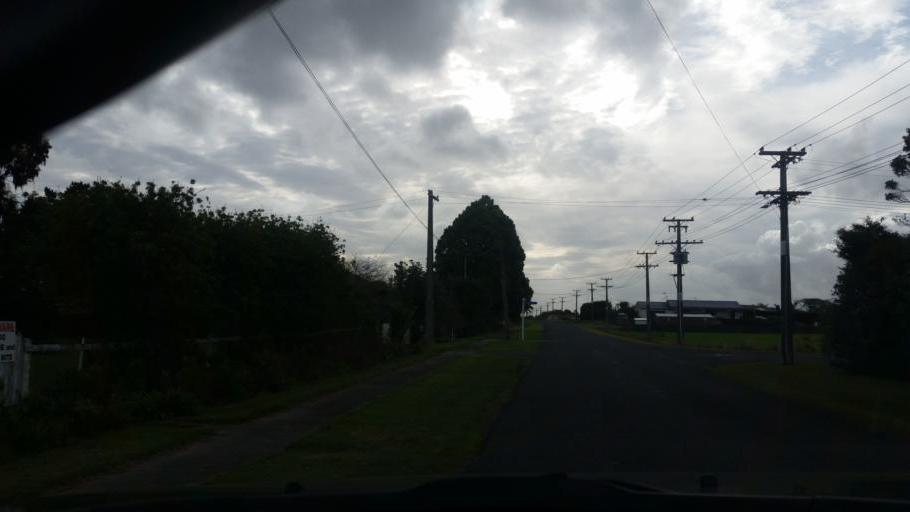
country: NZ
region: Northland
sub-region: Kaipara District
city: Dargaville
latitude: -36.0302
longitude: 173.9167
